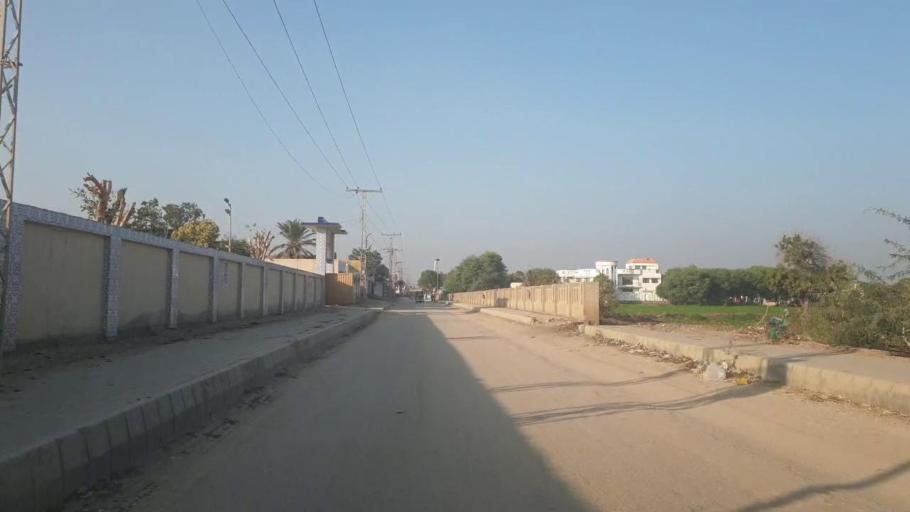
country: PK
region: Sindh
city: Jamshoro
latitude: 25.4371
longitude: 68.2906
